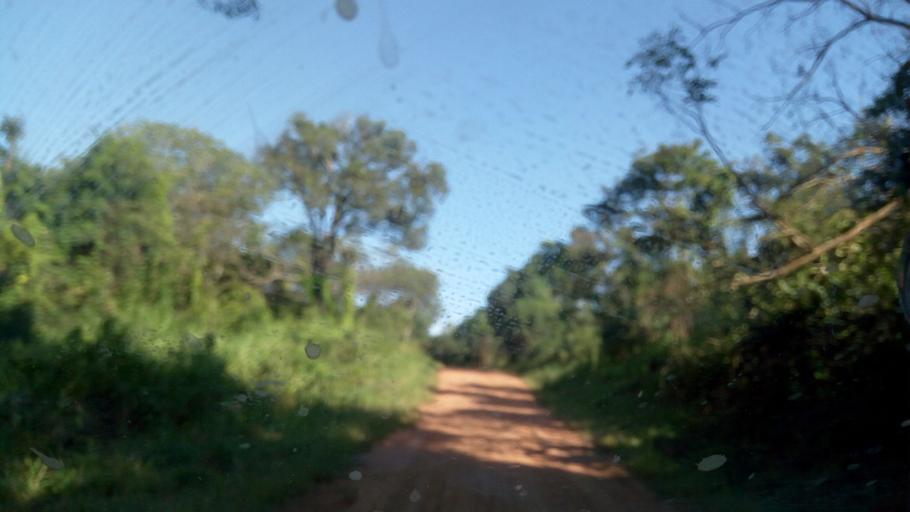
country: BI
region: Bururi
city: Rumonge
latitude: -4.3802
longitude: 28.9117
